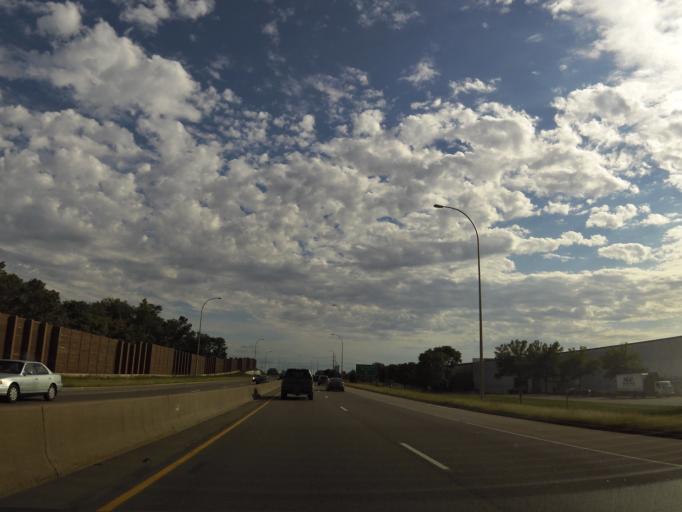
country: US
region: Minnesota
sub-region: Hennepin County
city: New Hope
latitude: 44.9975
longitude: -93.4010
